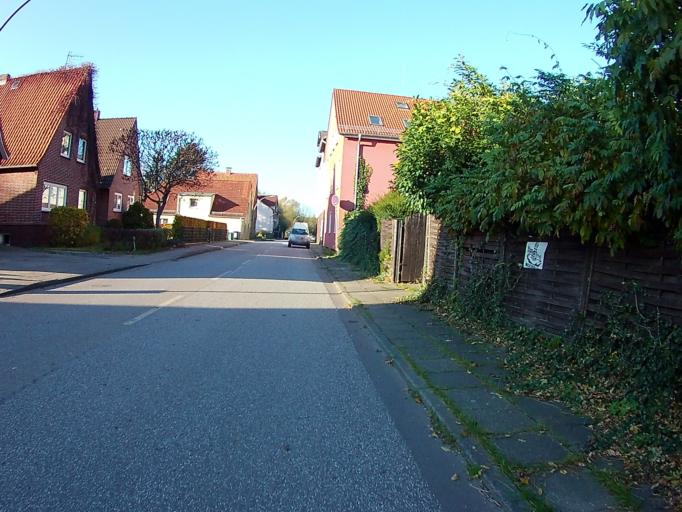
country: DE
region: Hamburg
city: Altona
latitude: 53.4915
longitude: 9.9334
